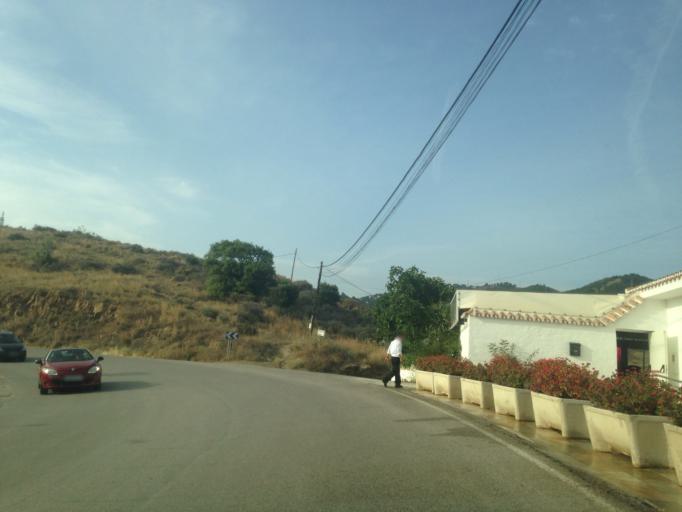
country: ES
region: Andalusia
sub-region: Provincia de Malaga
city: Malaga
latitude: 36.7487
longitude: -4.4073
